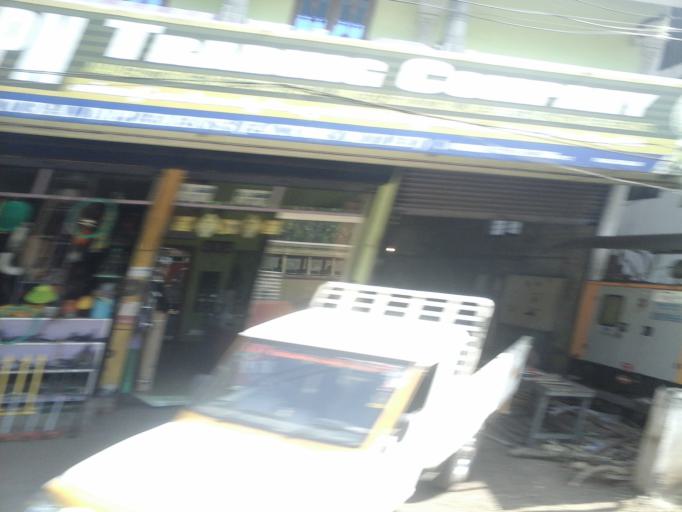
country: IN
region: Kerala
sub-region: Kottayam
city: Erattupetta
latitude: 9.7016
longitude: 76.7576
